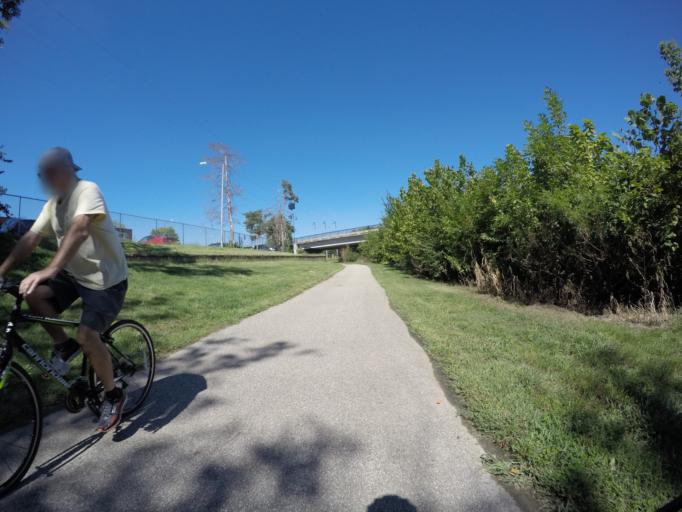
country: US
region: Kansas
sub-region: Johnson County
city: Leawood
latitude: 38.9350
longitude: -94.6343
